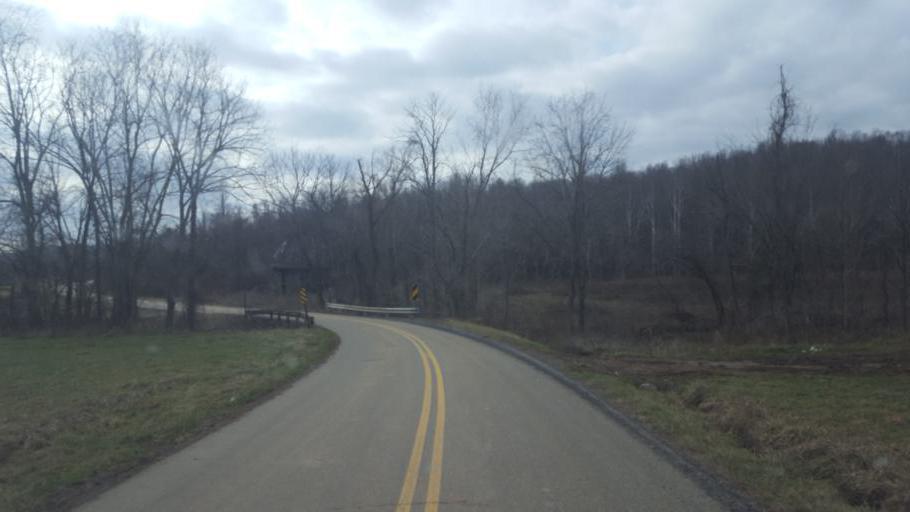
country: US
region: Ohio
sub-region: Gallia County
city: Gallipolis
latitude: 38.7284
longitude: -82.3225
